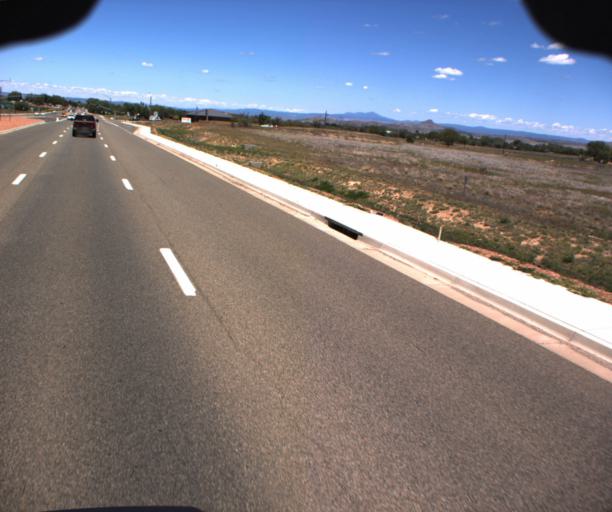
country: US
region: Arizona
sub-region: Yavapai County
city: Chino Valley
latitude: 34.7361
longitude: -112.4542
